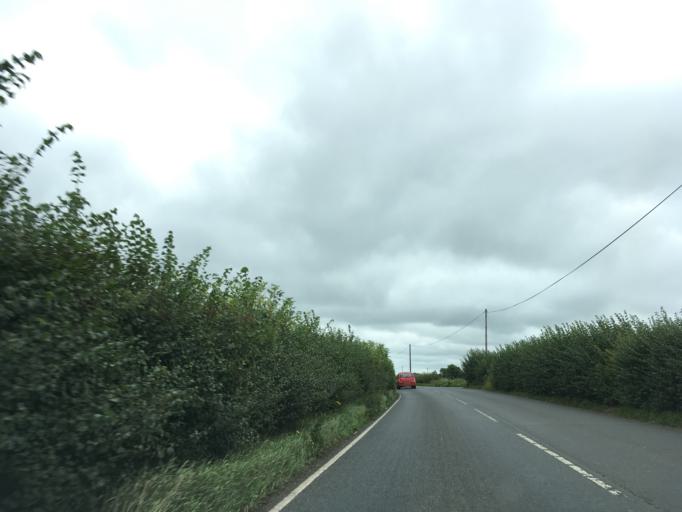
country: GB
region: England
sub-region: Bath and North East Somerset
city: Timsbury
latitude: 51.3528
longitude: -2.4848
